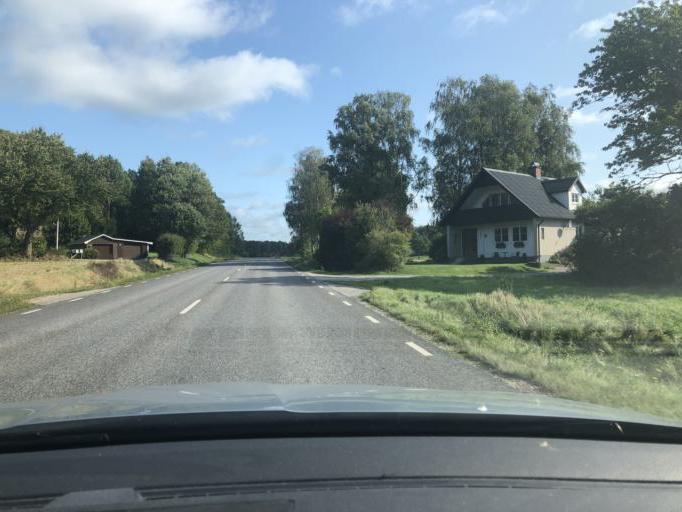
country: SE
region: Blekinge
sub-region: Olofstroms Kommun
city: Jamshog
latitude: 56.2454
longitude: 14.5479
